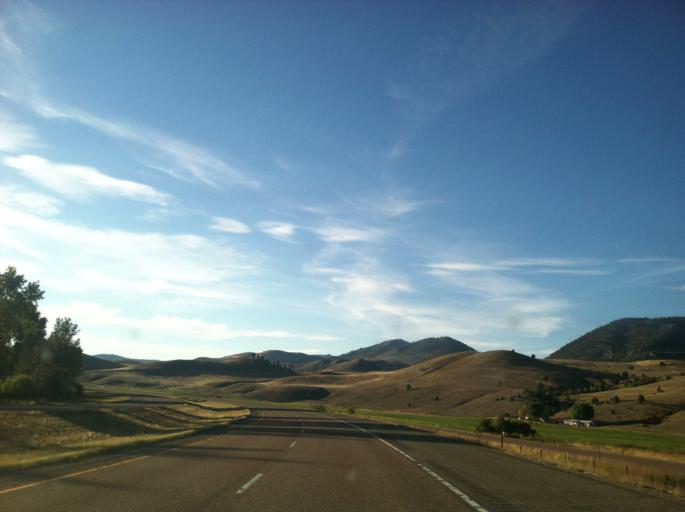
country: US
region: Montana
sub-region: Granite County
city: Philipsburg
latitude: 46.6962
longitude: -113.2070
